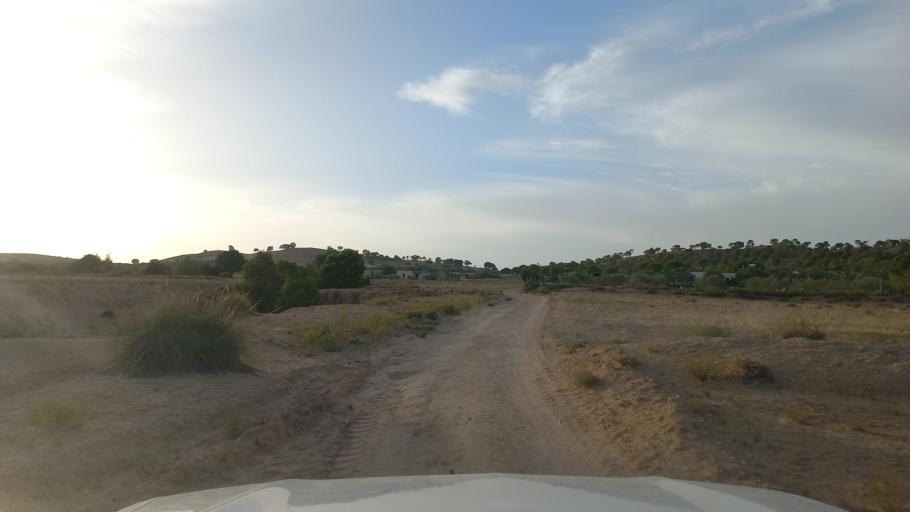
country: TN
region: Al Qasrayn
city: Sbiba
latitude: 35.4113
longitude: 8.9151
